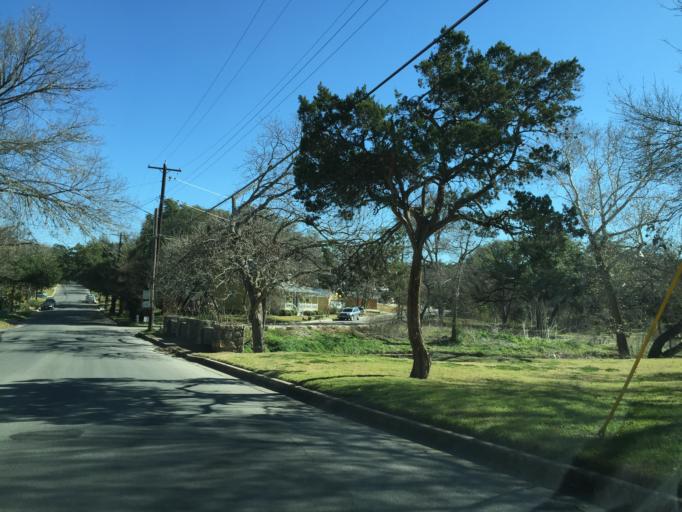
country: US
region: Texas
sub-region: Travis County
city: Austin
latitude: 30.2463
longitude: -97.7452
